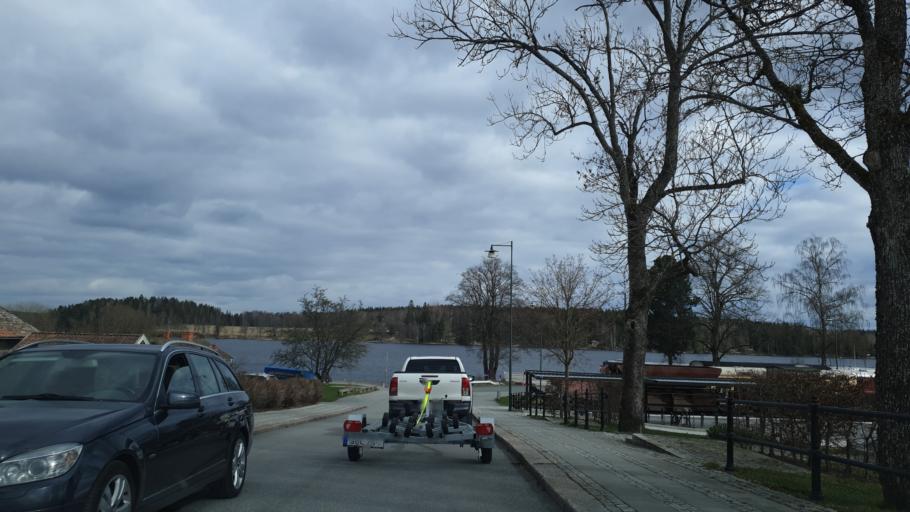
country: SE
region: OErebro
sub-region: Nora Kommun
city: Nora
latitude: 59.5179
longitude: 15.0413
